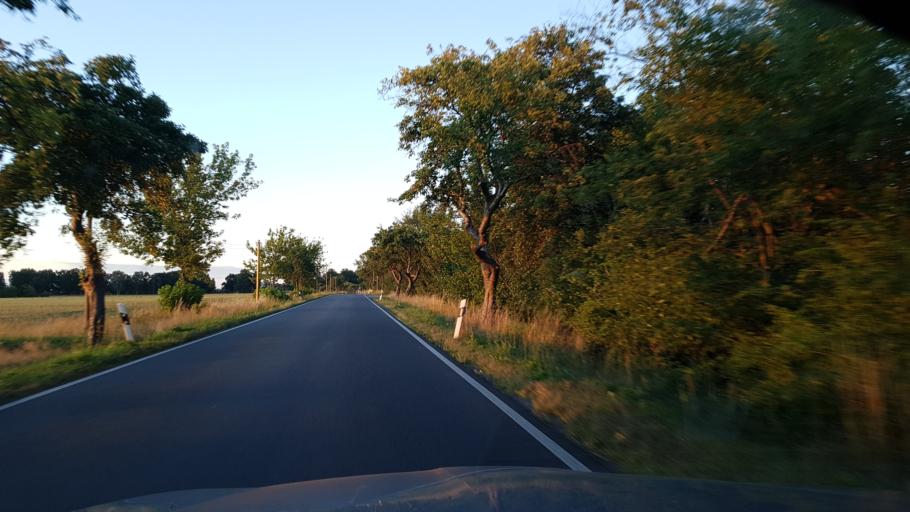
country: DE
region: Brandenburg
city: Groden
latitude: 51.4127
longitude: 13.5910
